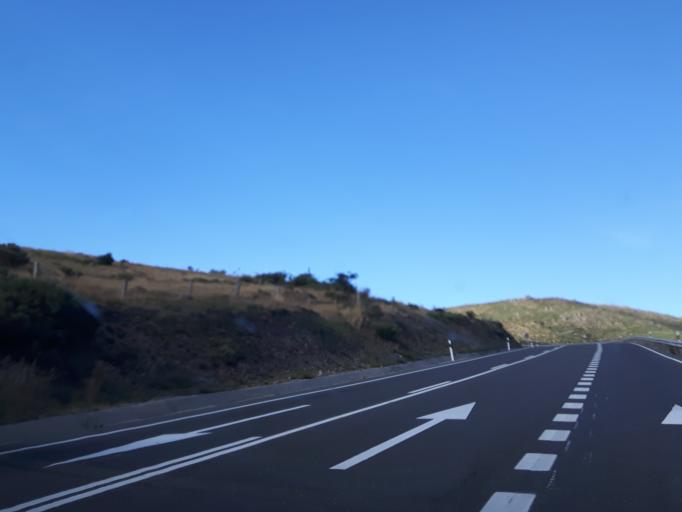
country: ES
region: Castille and Leon
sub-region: Provincia de Avila
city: Mengamunoz
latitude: 40.4904
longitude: -5.0075
